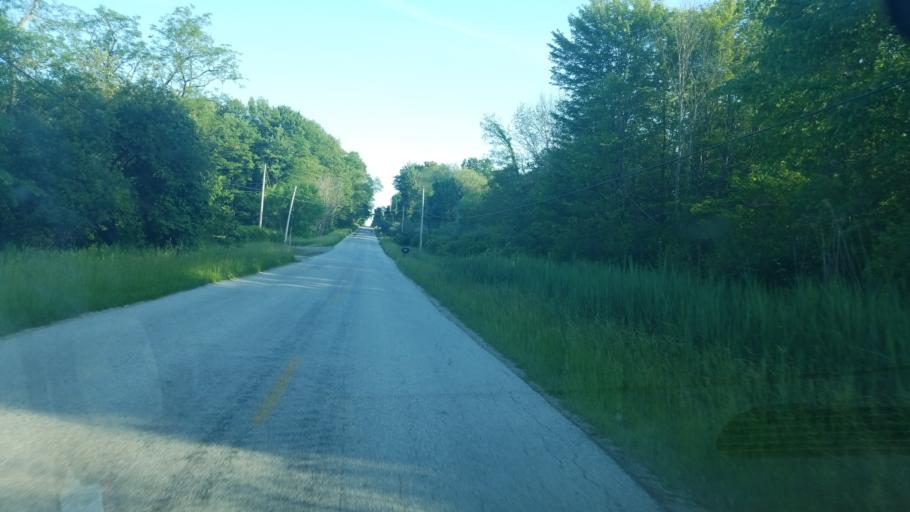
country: US
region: Ohio
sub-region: Portage County
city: Ravenna
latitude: 41.1251
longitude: -81.1460
